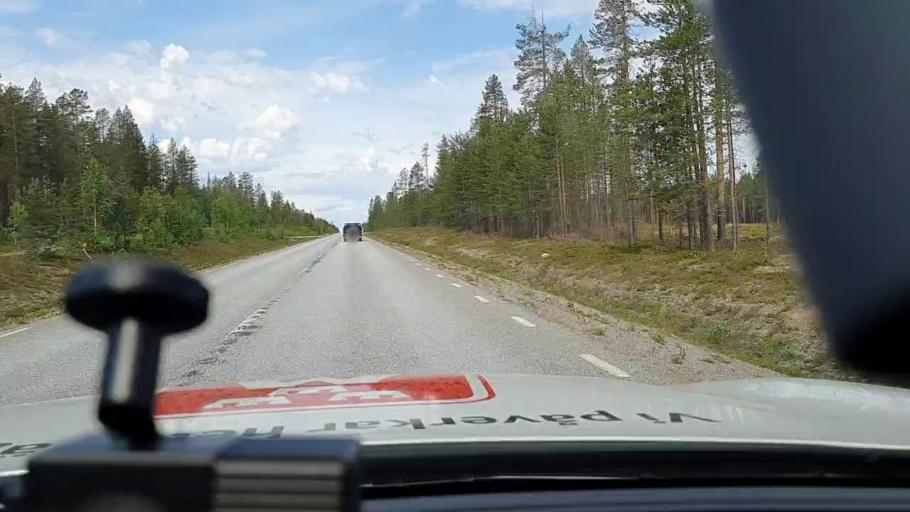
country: SE
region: Norrbotten
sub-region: Jokkmokks Kommun
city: Jokkmokk
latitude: 66.5228
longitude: 20.2065
